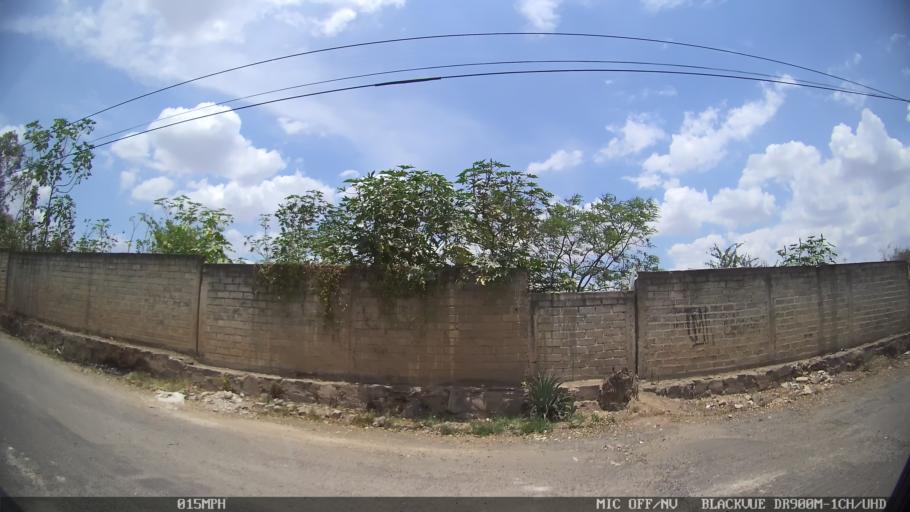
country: MX
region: Jalisco
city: Tonala
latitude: 20.6276
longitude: -103.2259
